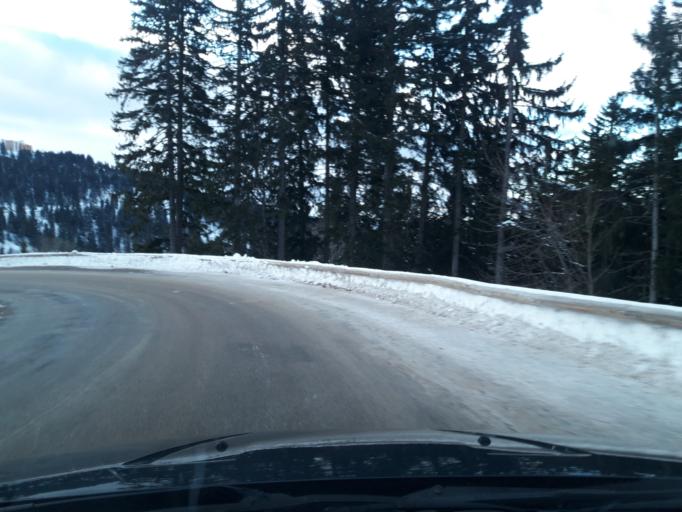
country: FR
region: Rhone-Alpes
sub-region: Departement de l'Isere
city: Vaulnaveys-le-Bas
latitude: 45.1256
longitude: 5.8723
